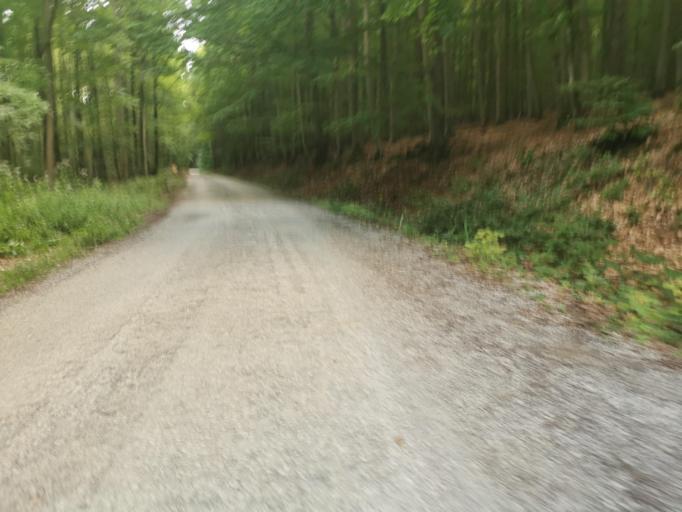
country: SK
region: Trenciansky
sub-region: Okres Myjava
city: Myjava
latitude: 48.7928
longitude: 17.6077
